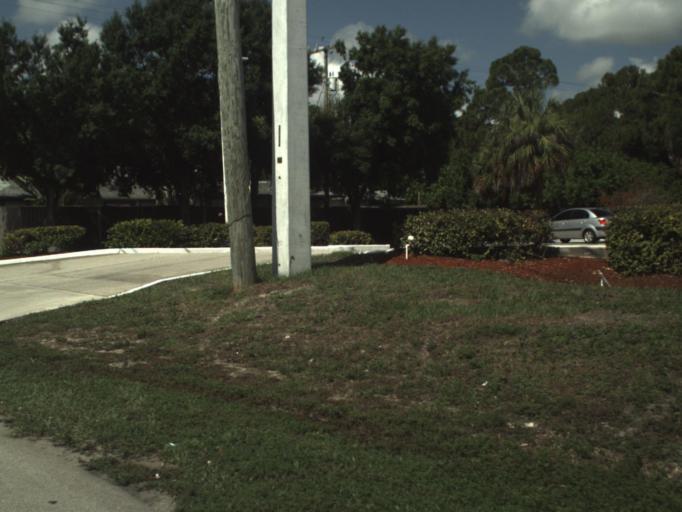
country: US
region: Florida
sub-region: Saint Lucie County
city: Port Saint Lucie
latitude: 27.2580
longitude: -80.3751
